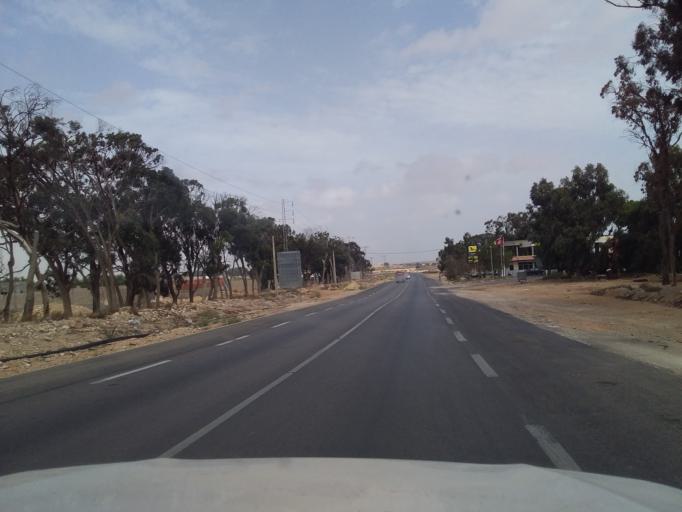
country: TN
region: Qabis
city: Gabes
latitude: 33.6365
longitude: 10.2824
